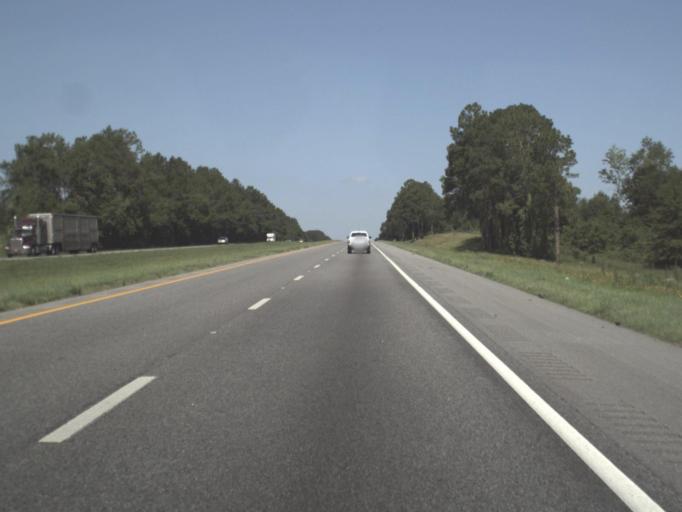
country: US
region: Florida
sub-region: Suwannee County
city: Live Oak
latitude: 30.3500
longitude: -83.0061
